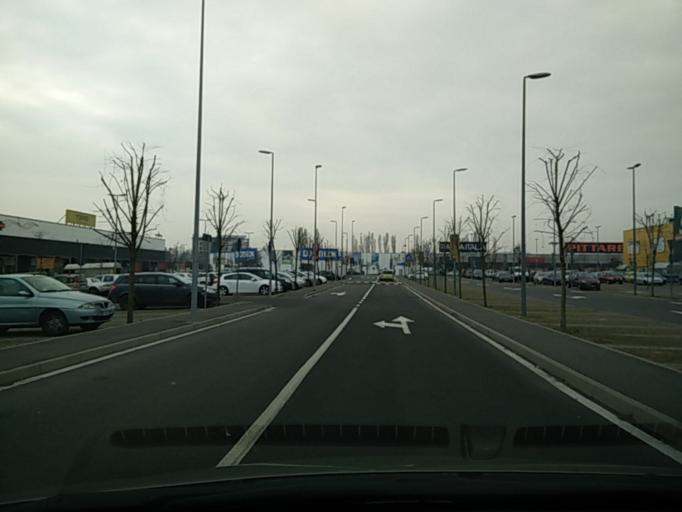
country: IT
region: Piedmont
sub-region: Provincia di Torino
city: Settimo Torinese
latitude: 45.1395
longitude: 7.7323
